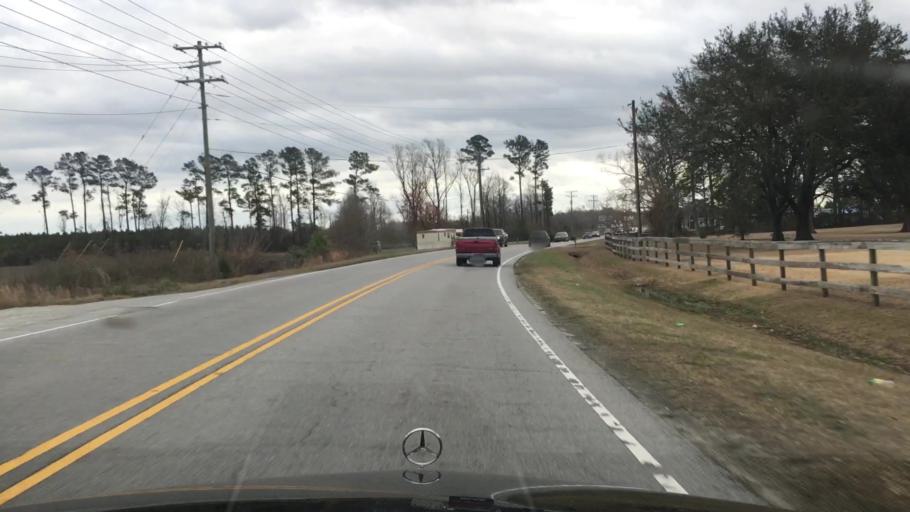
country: US
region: North Carolina
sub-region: Onslow County
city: Half Moon
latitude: 34.8516
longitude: -77.4826
